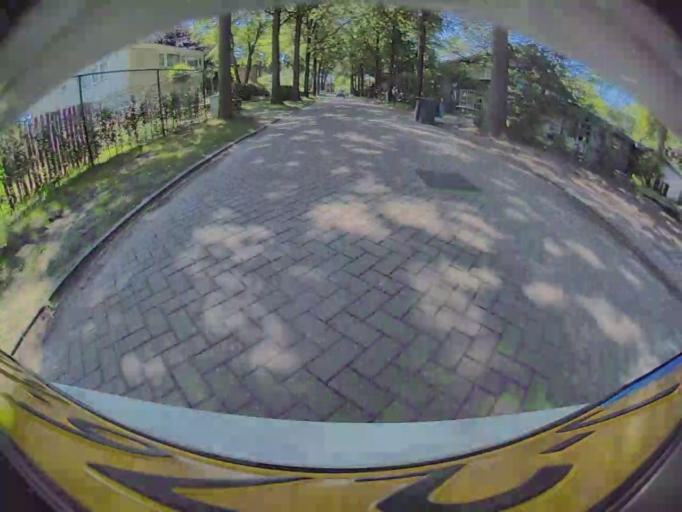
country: NL
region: North Brabant
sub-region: Gemeente 's-Hertogenbosch
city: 's-Hertogenbosch
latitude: 51.7077
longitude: 5.3672
